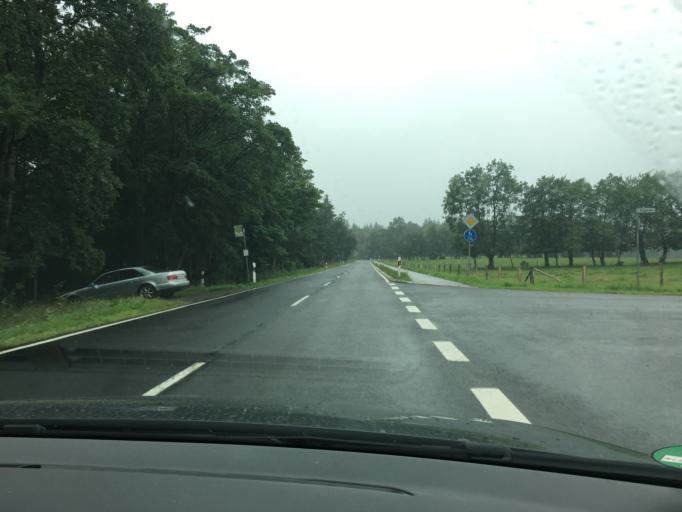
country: DE
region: North Rhine-Westphalia
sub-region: Regierungsbezirk Koln
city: Simmerath
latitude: 50.6719
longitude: 6.3021
